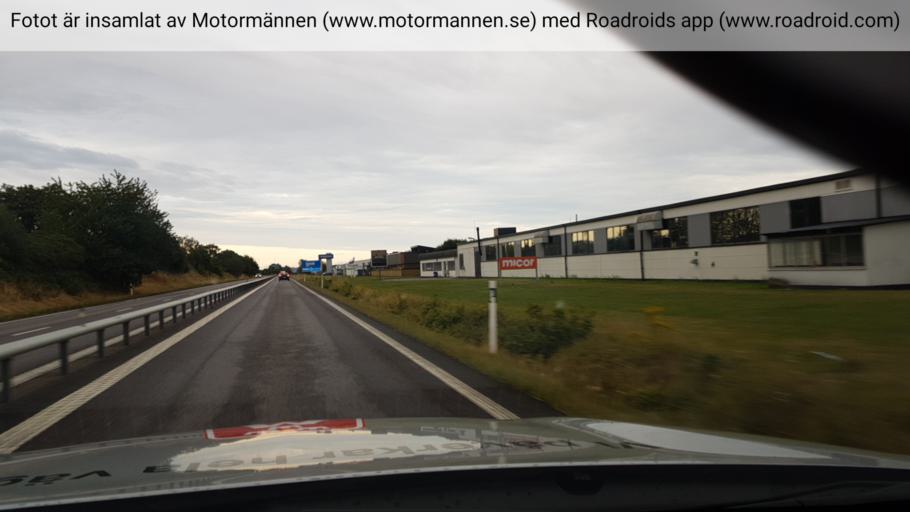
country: SE
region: Halland
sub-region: Laholms Kommun
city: Laholm
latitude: 56.5016
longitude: 13.0245
